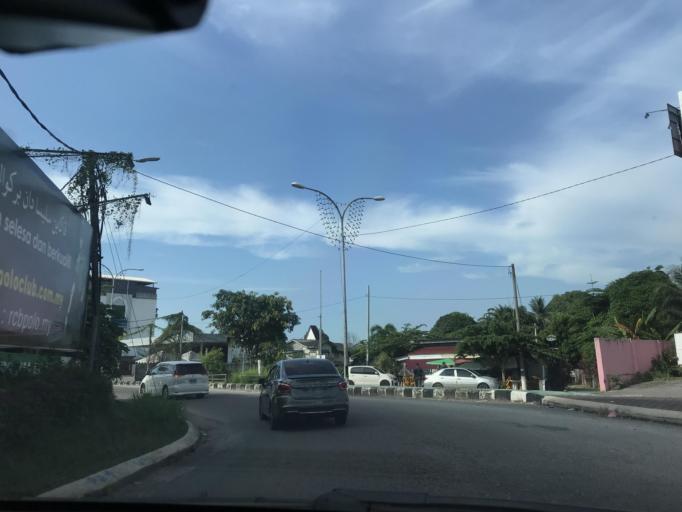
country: MY
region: Kelantan
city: Kota Bharu
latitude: 6.1165
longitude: 102.2470
